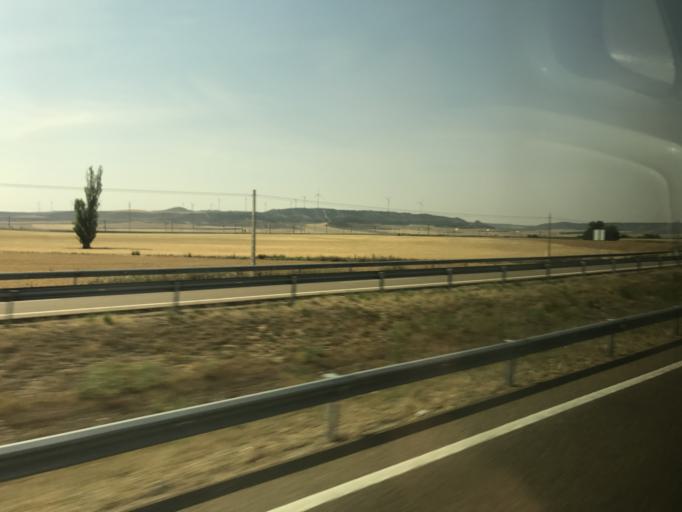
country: ES
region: Castille and Leon
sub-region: Provincia de Palencia
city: Quintana del Puente
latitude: 42.0637
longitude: -4.2306
